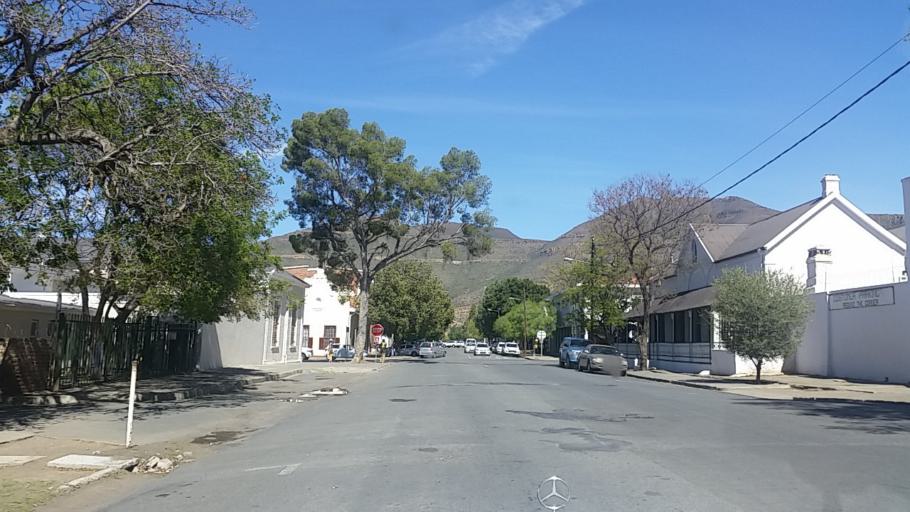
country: ZA
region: Eastern Cape
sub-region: Cacadu District Municipality
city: Graaff-Reinet
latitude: -32.2508
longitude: 24.5362
